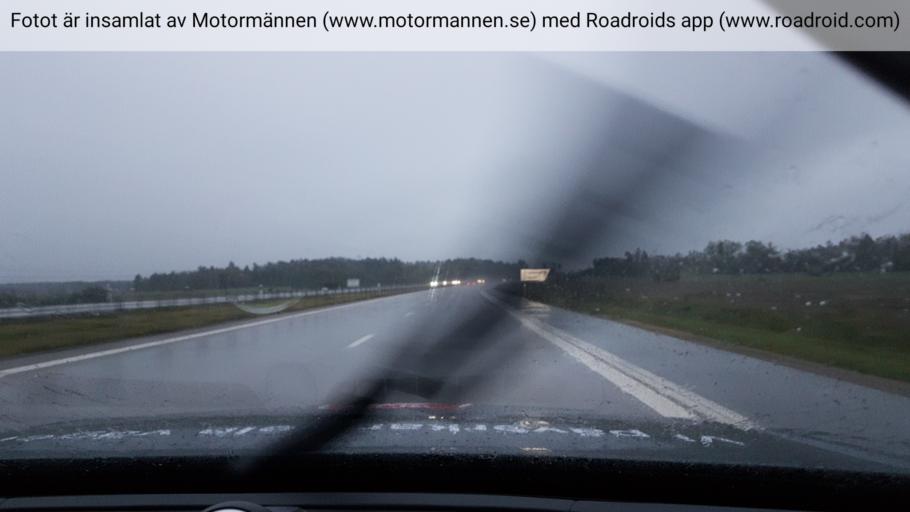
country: SE
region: Uppsala
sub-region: Uppsala Kommun
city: Storvreta
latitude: 59.9769
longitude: 17.6431
